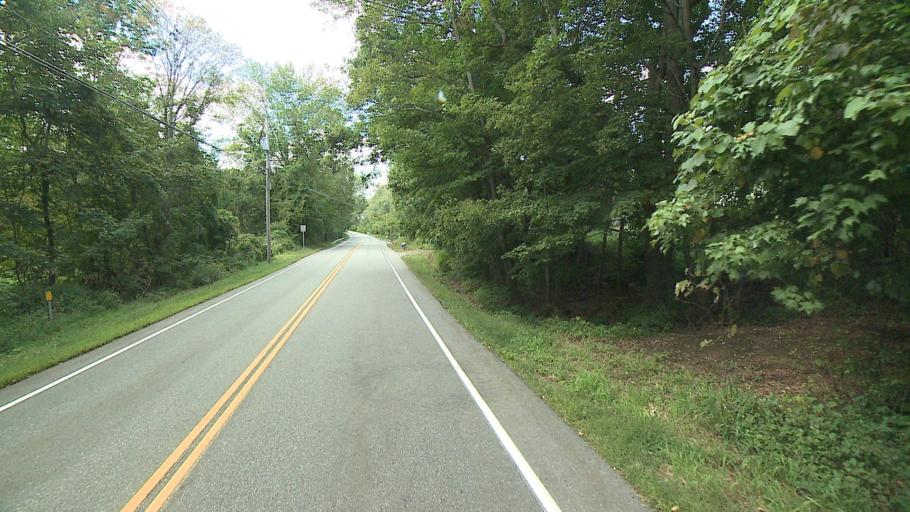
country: US
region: Connecticut
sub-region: Tolland County
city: Storrs
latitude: 41.8432
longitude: -72.2163
